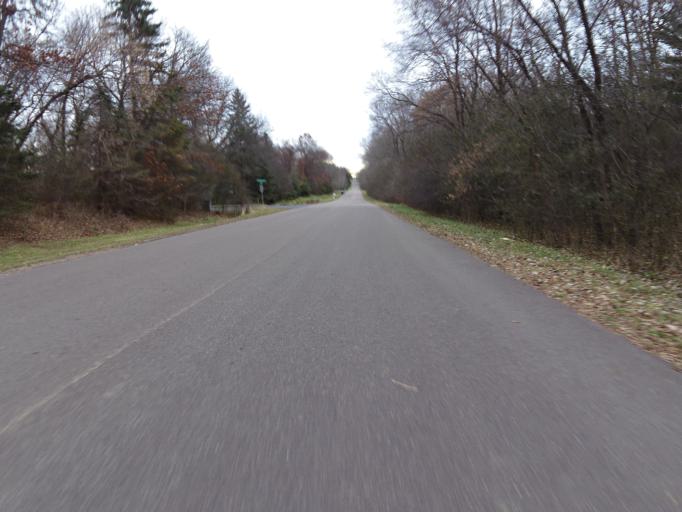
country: US
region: Minnesota
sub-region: Washington County
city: Lake Elmo
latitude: 44.9847
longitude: -92.8730
